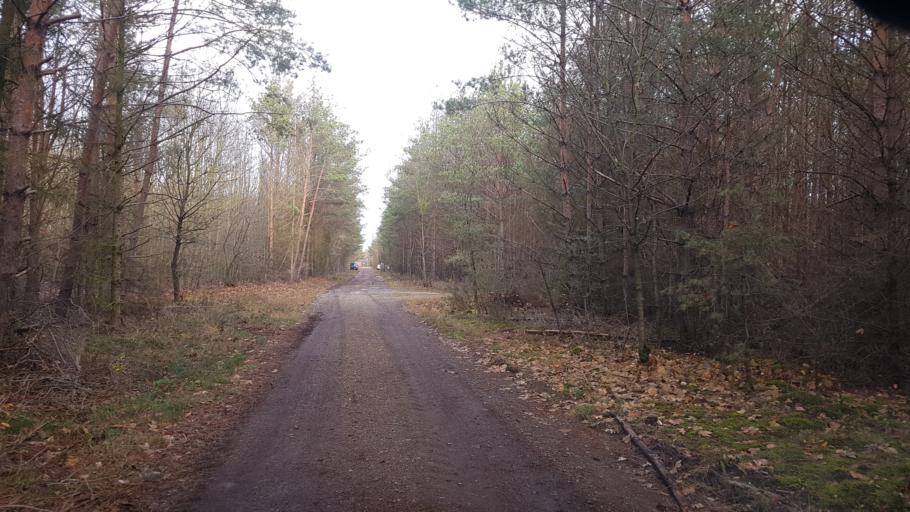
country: DE
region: Brandenburg
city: Falkenberg
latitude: 51.5383
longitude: 13.2059
